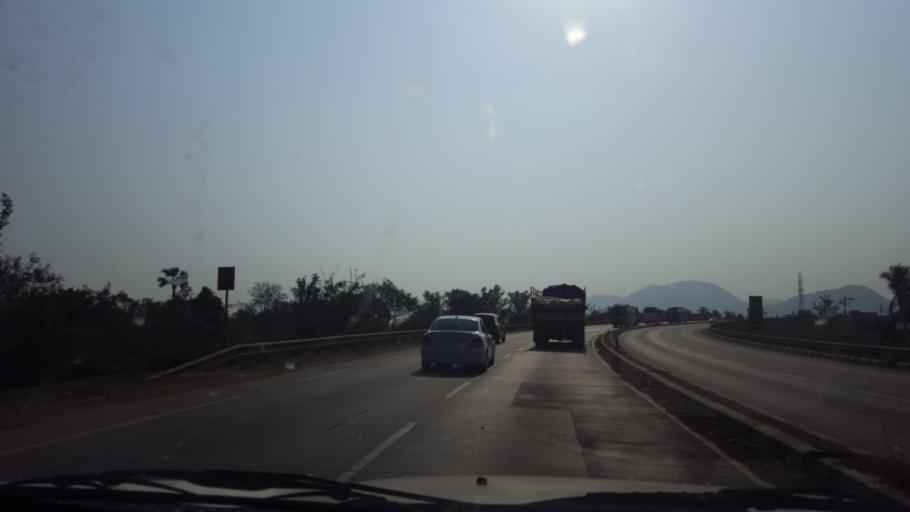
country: IN
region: Andhra Pradesh
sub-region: Vishakhapatnam
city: Anakapalle
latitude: 17.6512
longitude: 82.9239
